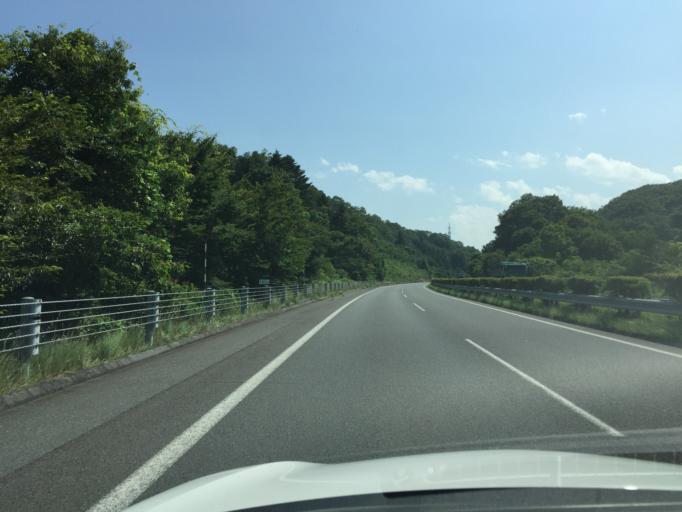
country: JP
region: Fukushima
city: Iwaki
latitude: 36.9733
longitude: 140.7936
